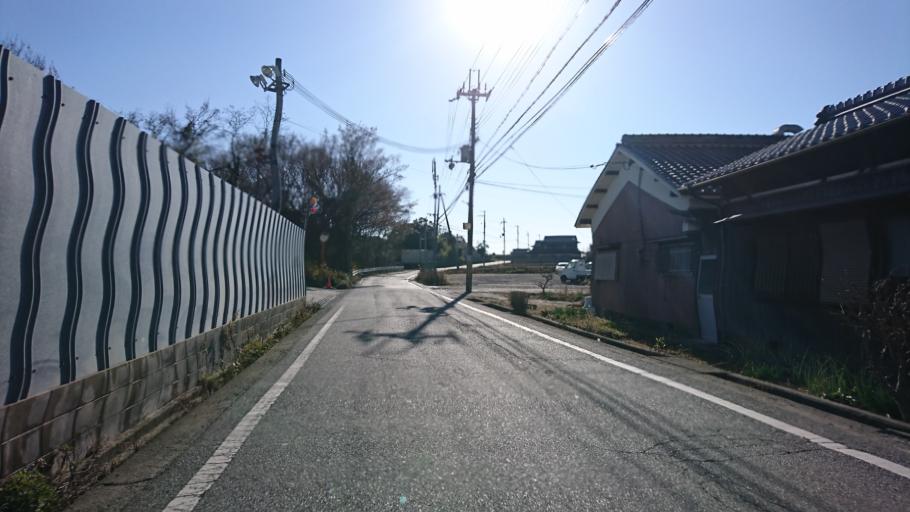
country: JP
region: Hyogo
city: Miki
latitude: 34.7412
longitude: 134.9424
